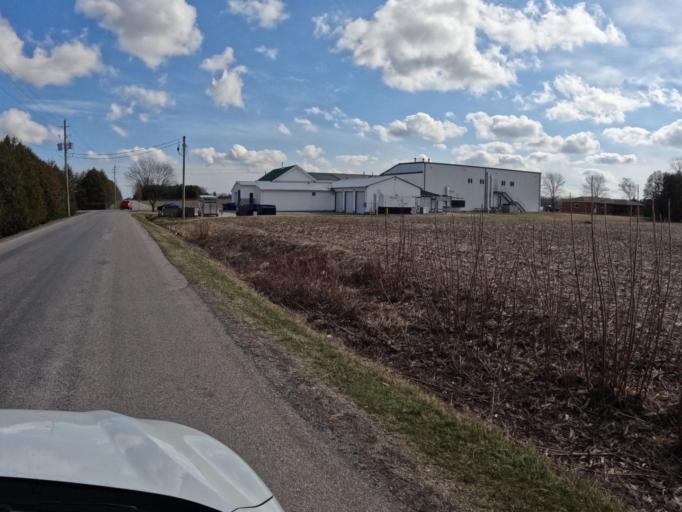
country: CA
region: Ontario
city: Norfolk County
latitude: 42.8645
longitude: -80.2754
